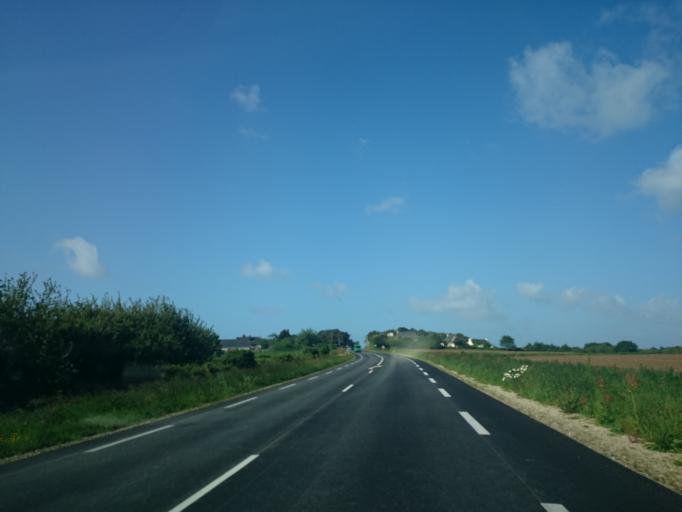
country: FR
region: Brittany
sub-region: Departement du Morbihan
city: Larmor-Baden
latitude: 47.6161
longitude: -2.8791
